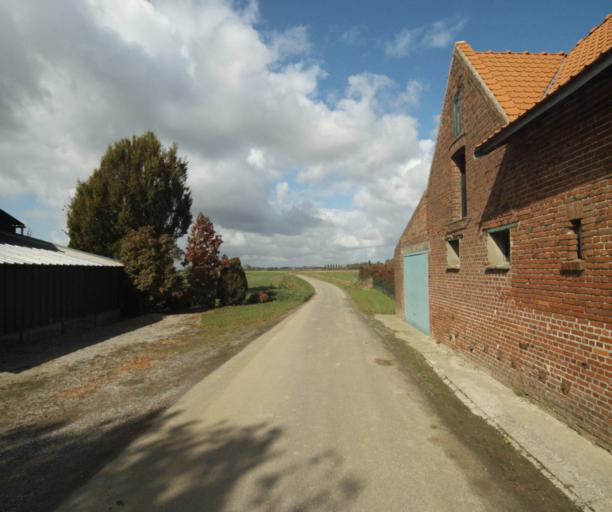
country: FR
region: Nord-Pas-de-Calais
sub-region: Departement du Nord
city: Perenchies
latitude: 50.6926
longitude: 2.9576
